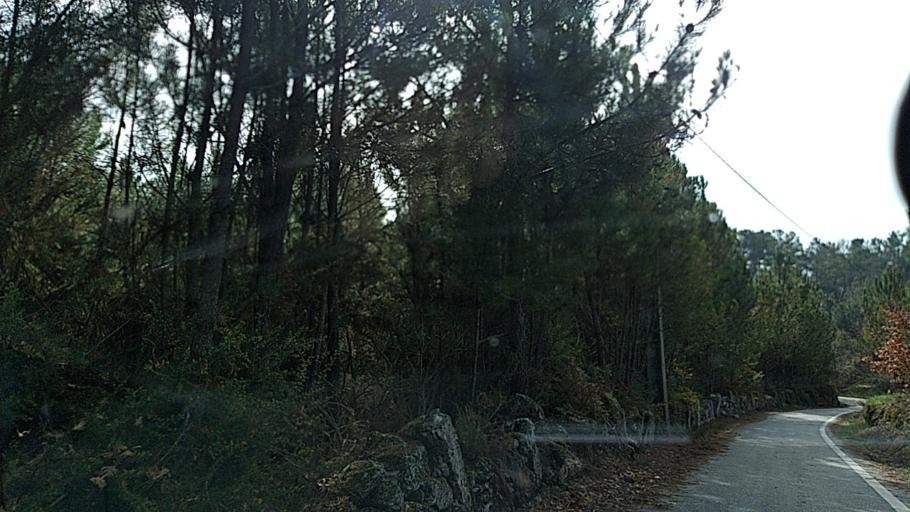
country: PT
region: Guarda
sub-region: Fornos de Algodres
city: Fornos de Algodres
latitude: 40.6359
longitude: -7.5384
